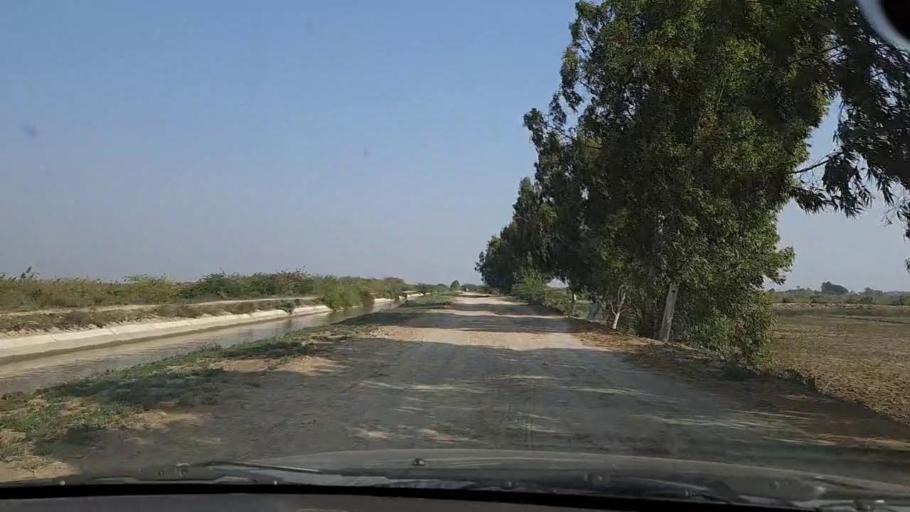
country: PK
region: Sindh
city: Mirpur Sakro
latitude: 24.3419
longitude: 67.7062
